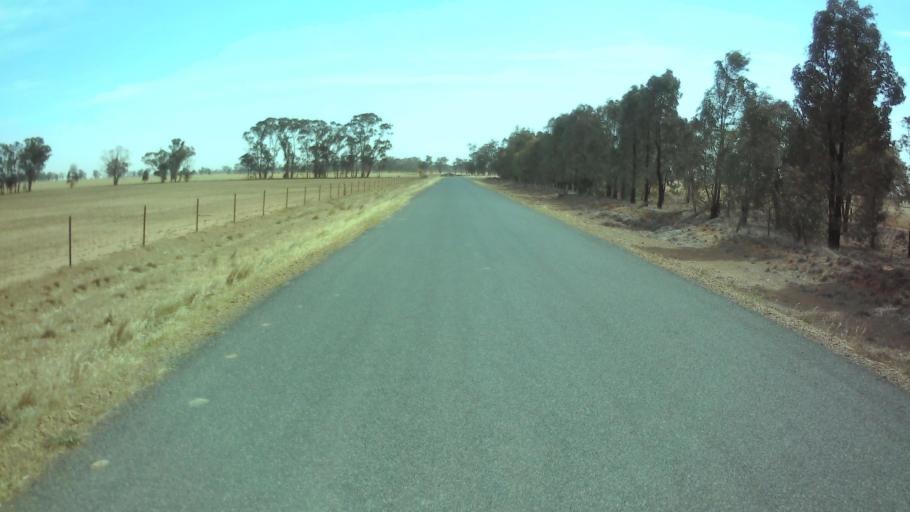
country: AU
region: New South Wales
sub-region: Weddin
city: Grenfell
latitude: -33.7110
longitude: 148.0017
